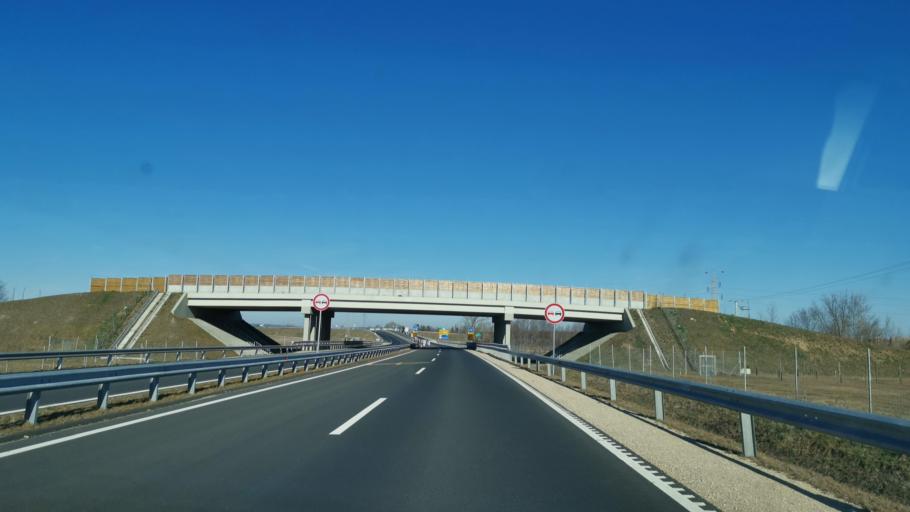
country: HU
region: Somogy
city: Balatonbereny
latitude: 46.6823
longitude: 17.2930
